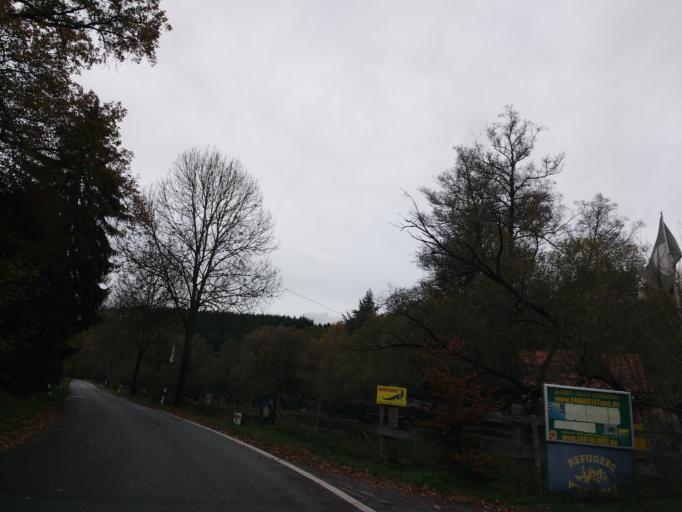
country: DE
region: Hesse
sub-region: Regierungsbezirk Kassel
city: Vohl
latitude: 51.1966
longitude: 8.9493
